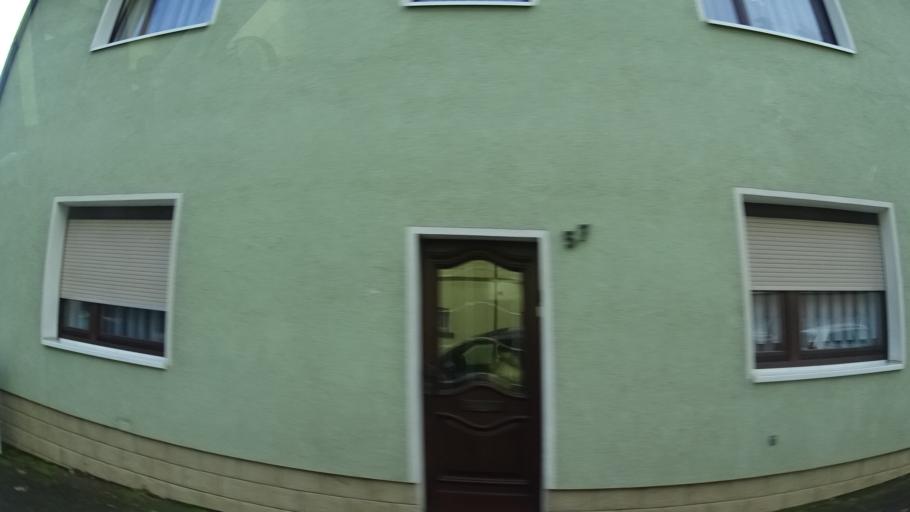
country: DE
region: Thuringia
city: Grafenhain
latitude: 50.8139
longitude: 10.6937
